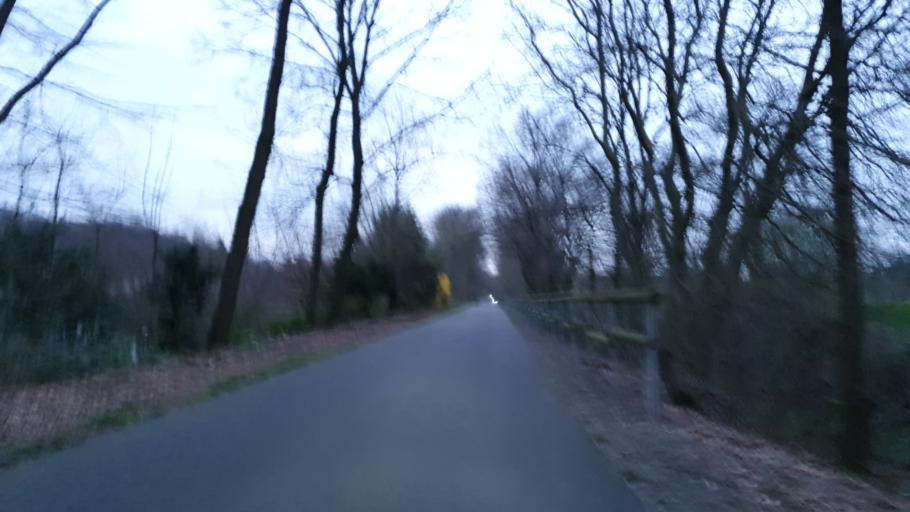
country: DE
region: North Rhine-Westphalia
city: Leichlingen
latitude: 51.0835
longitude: 7.0474
